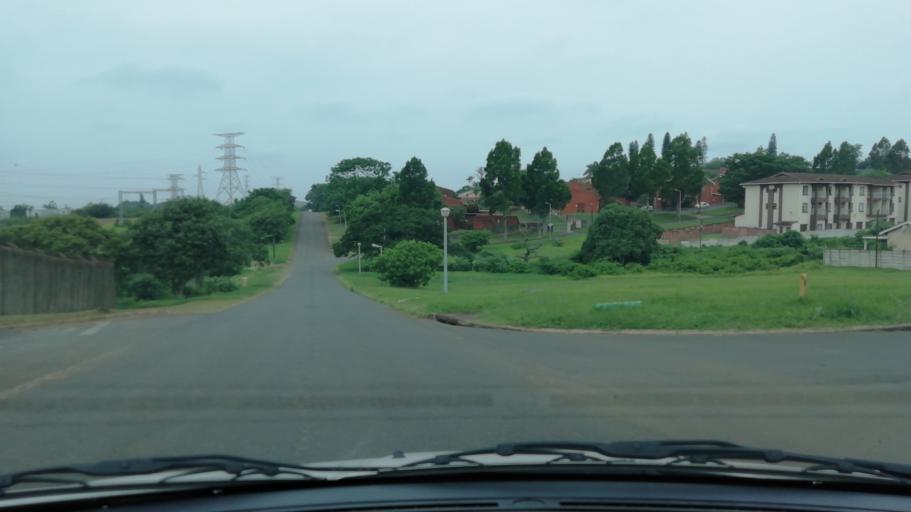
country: ZA
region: KwaZulu-Natal
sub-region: uThungulu District Municipality
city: Empangeni
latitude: -28.7392
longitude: 31.8848
